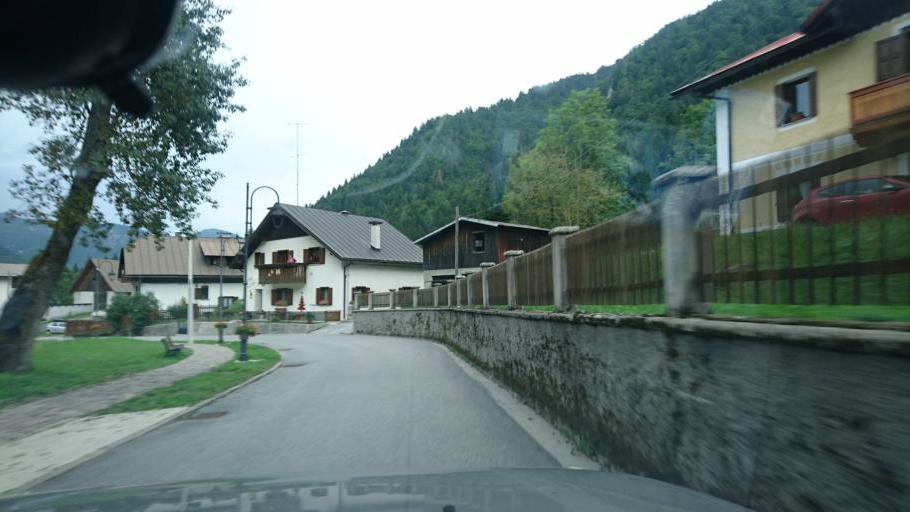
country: IT
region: Friuli Venezia Giulia
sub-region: Provincia di Udine
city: Malborghetto
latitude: 46.4887
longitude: 13.4910
